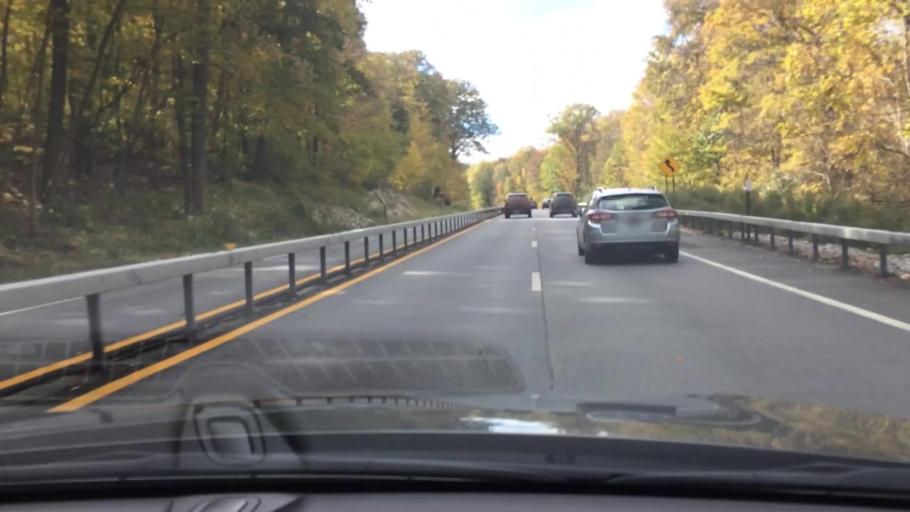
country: US
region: New York
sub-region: Dutchess County
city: Brinckerhoff
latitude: 41.4982
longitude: -73.7977
